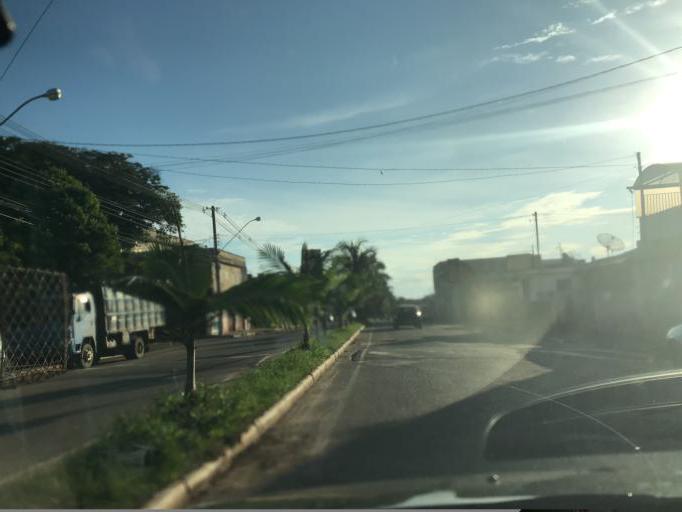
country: BR
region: Minas Gerais
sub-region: Tres Coracoes
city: Tres Coracoes
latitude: -21.6914
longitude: -45.2401
